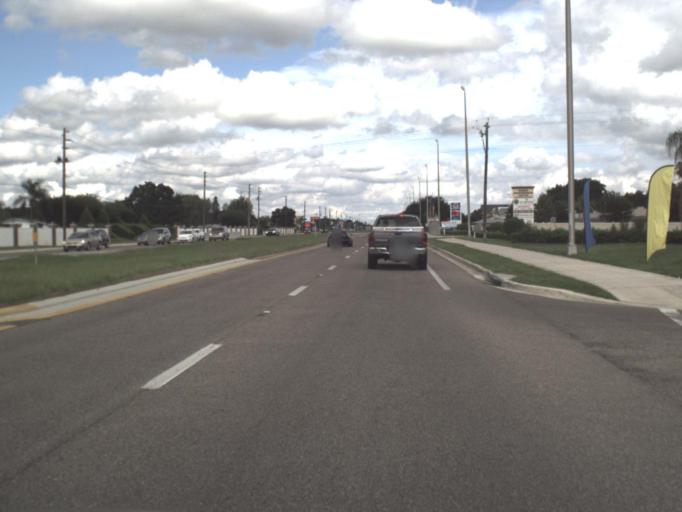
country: US
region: Florida
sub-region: Manatee County
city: Ellenton
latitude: 27.5389
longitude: -82.4846
